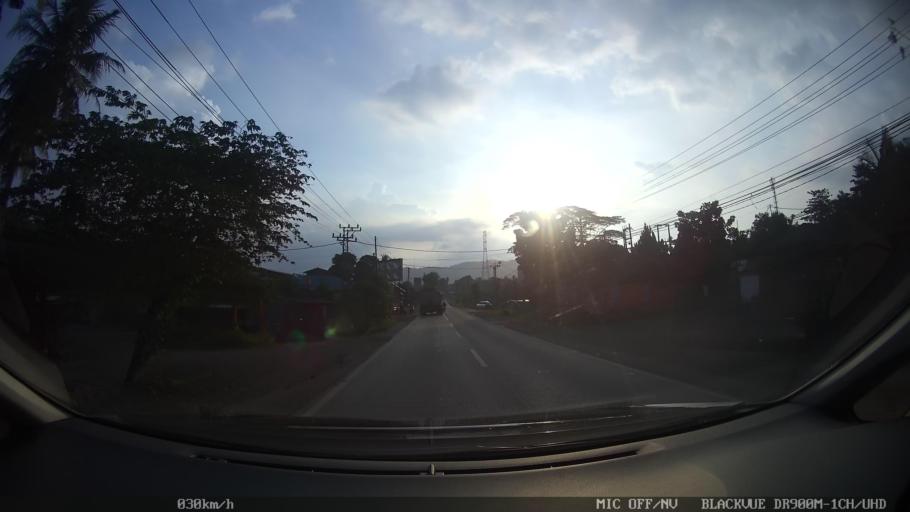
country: ID
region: Lampung
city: Panjang
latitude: -5.4197
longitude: 105.3380
